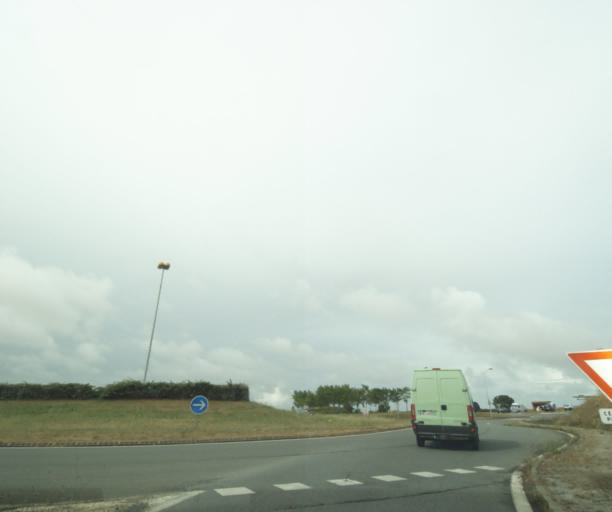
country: FR
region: Poitou-Charentes
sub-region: Departement de la Charente-Maritime
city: Marsilly
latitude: 46.2111
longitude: -1.1352
